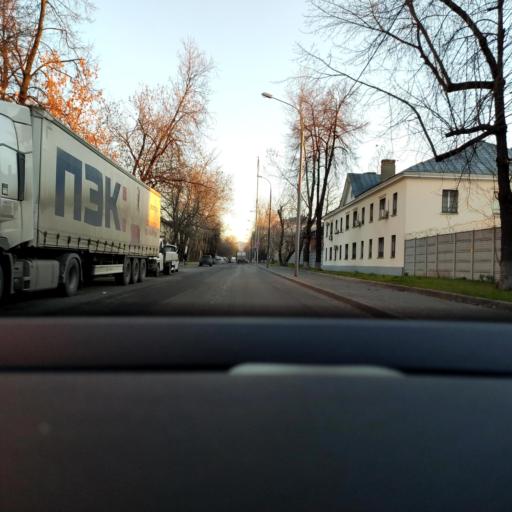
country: RU
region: Moscow
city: Ryazanskiy
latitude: 55.7197
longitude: 37.7534
